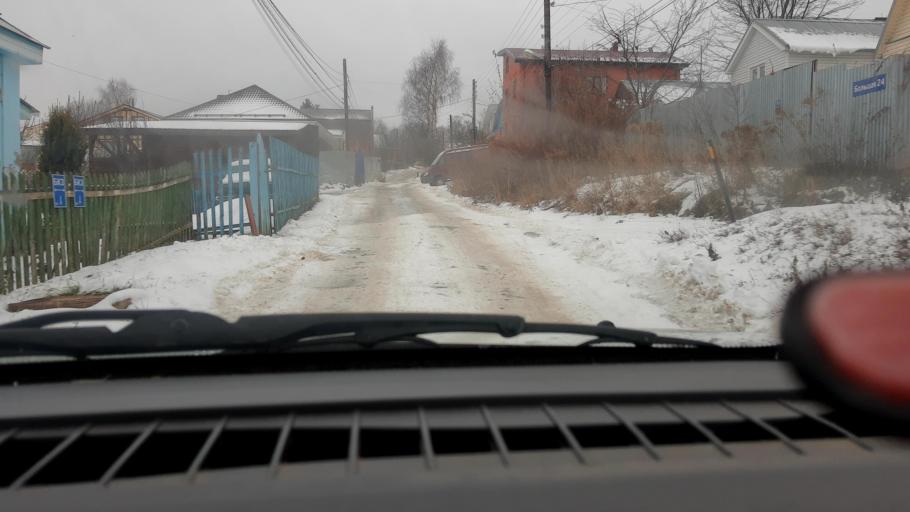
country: RU
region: Nizjnij Novgorod
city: Nizhniy Novgorod
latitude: 56.2329
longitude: 43.9830
